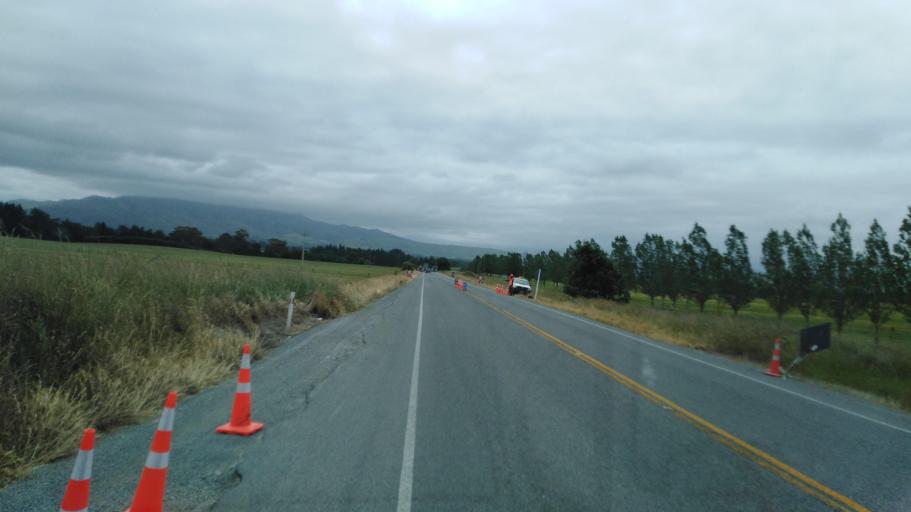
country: NZ
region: Canterbury
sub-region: Kaikoura District
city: Kaikoura
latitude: -42.7594
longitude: 173.2764
